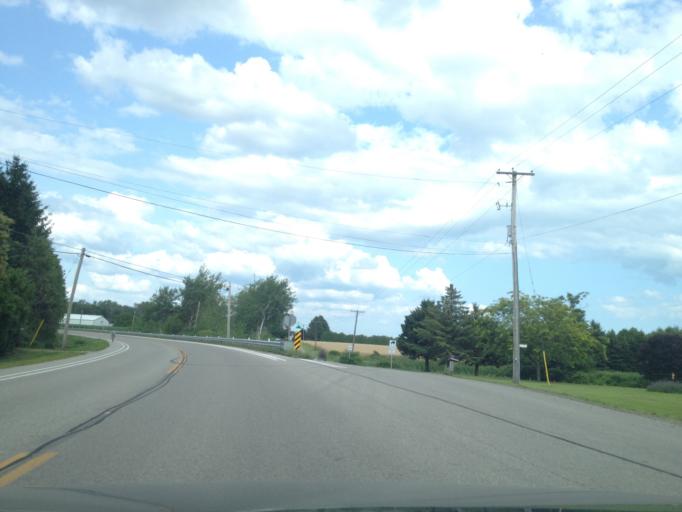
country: CA
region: Ontario
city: Aylmer
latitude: 42.6645
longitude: -80.9910
